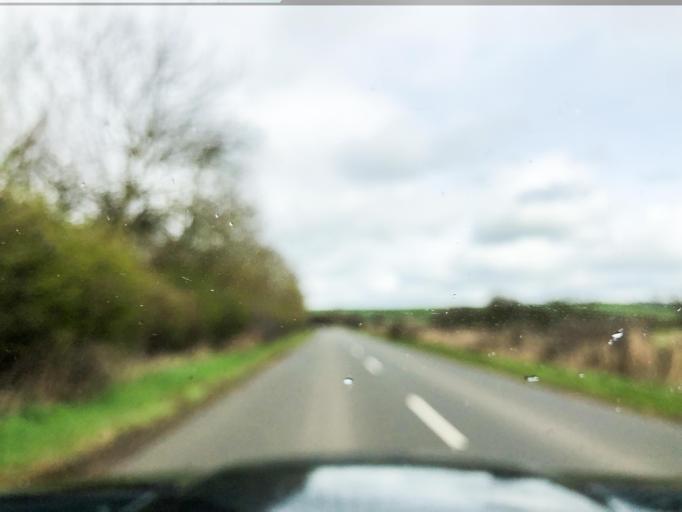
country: GB
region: England
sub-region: Warwickshire
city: Harbury
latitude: 52.1484
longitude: -1.4402
